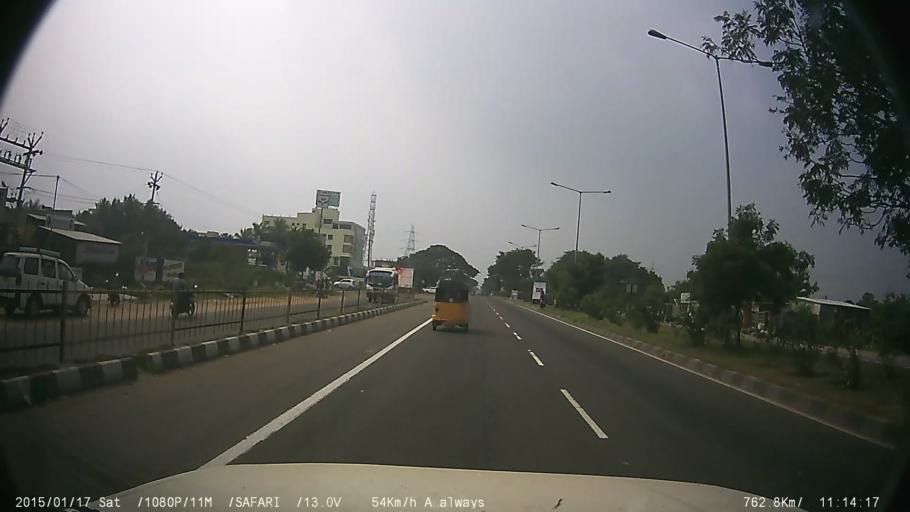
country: IN
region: Tamil Nadu
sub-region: Kancheepuram
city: Madambakkam
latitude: 12.8075
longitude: 80.0284
